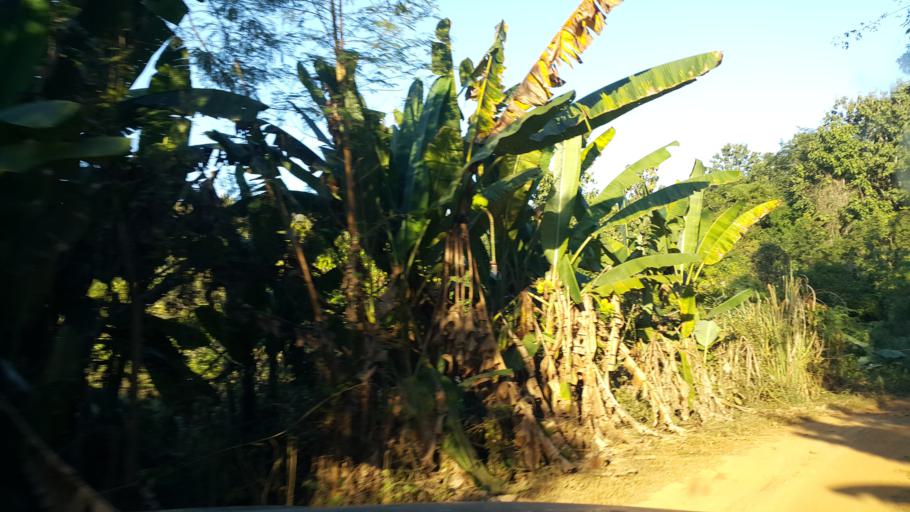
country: TH
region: Sukhothai
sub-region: Amphoe Si Satchanalai
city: Si Satchanalai
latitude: 17.5843
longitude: 99.6036
